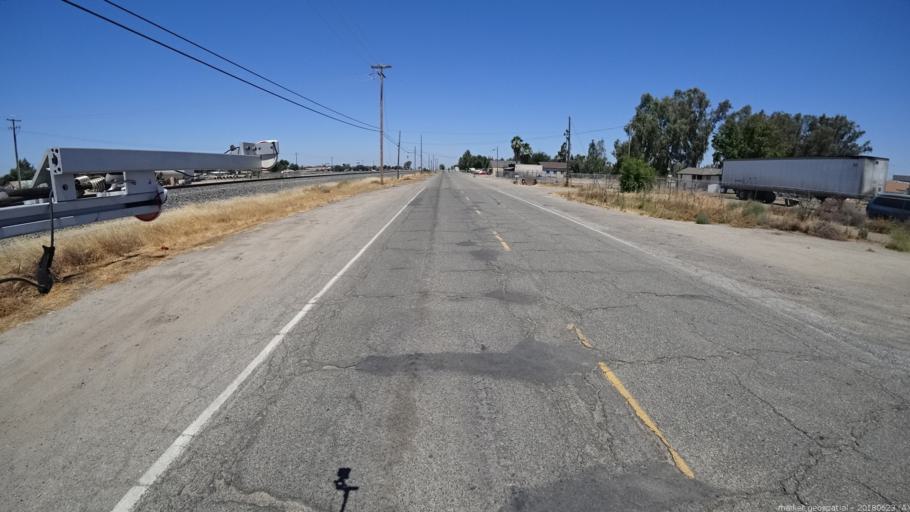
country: US
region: California
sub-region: Madera County
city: Chowchilla
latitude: 37.1211
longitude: -120.2523
